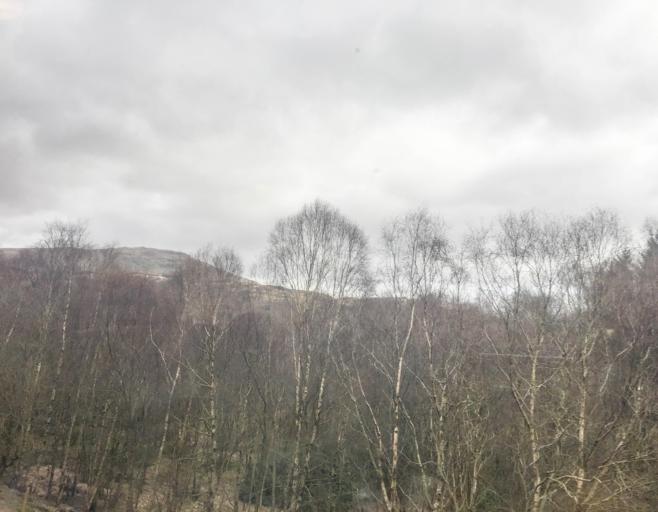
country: GB
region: Scotland
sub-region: Argyll and Bute
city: Garelochhead
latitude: 56.2533
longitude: -4.7106
